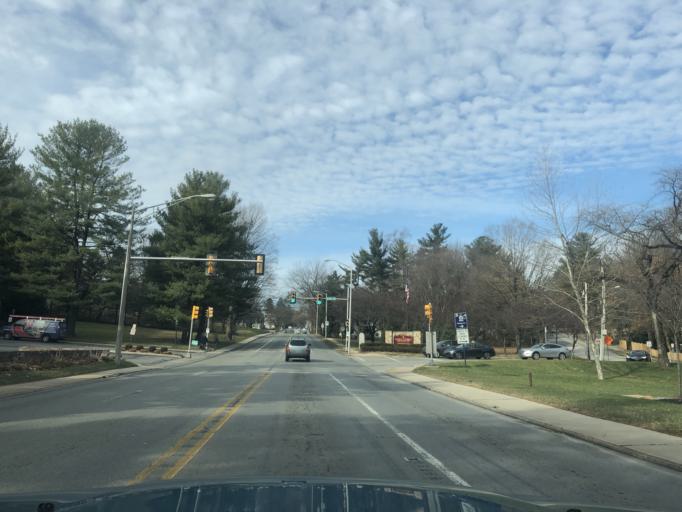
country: US
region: Pennsylvania
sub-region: Montgomery County
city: Bryn Mawr
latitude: 40.0270
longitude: -75.3292
